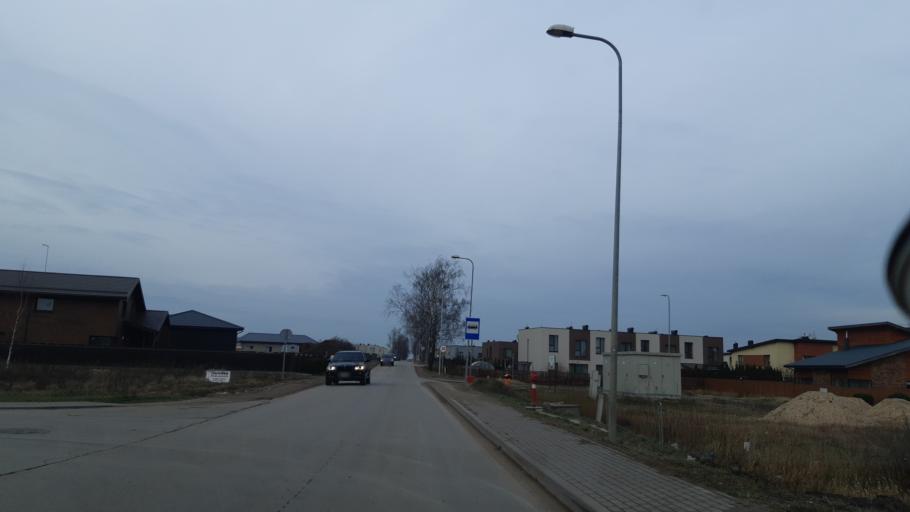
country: LT
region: Kauno apskritis
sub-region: Kauno rajonas
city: Akademija (Kaunas)
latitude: 54.9453
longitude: 23.8287
